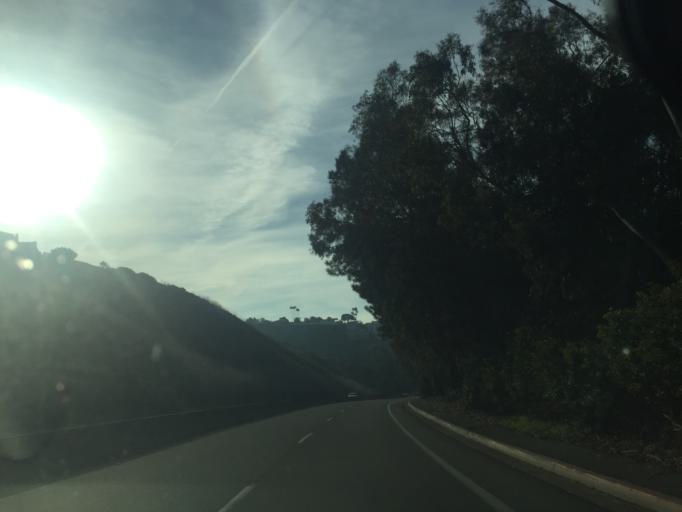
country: US
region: California
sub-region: San Diego County
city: La Jolla
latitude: 32.8569
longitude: -117.2459
